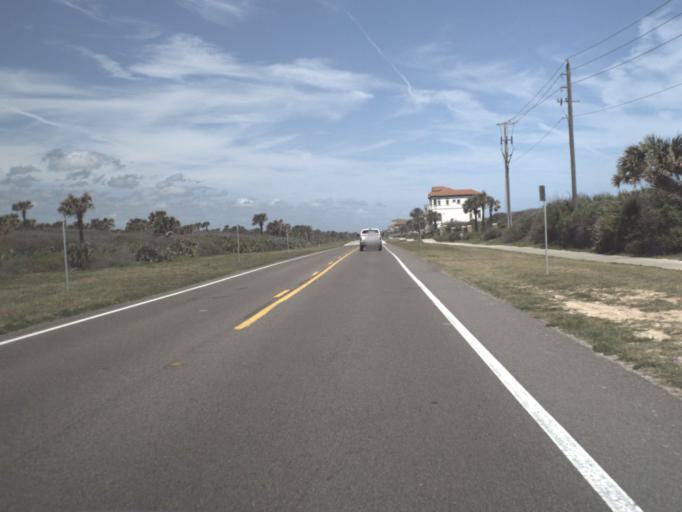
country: US
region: Florida
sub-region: Flagler County
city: Palm Coast
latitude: 29.5514
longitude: -81.1627
